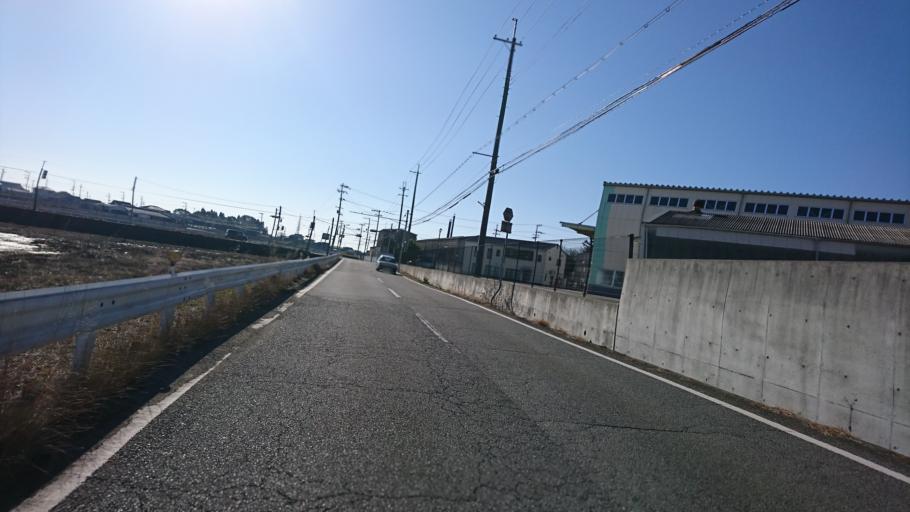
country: JP
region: Hyogo
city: Miki
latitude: 34.7527
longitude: 134.9257
